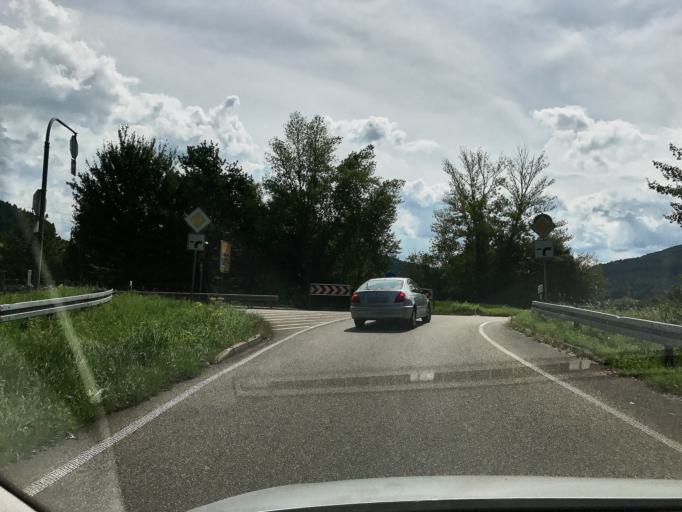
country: DE
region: Baden-Wuerttemberg
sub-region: Freiburg Region
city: Steinach
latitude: 48.2859
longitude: 8.0743
